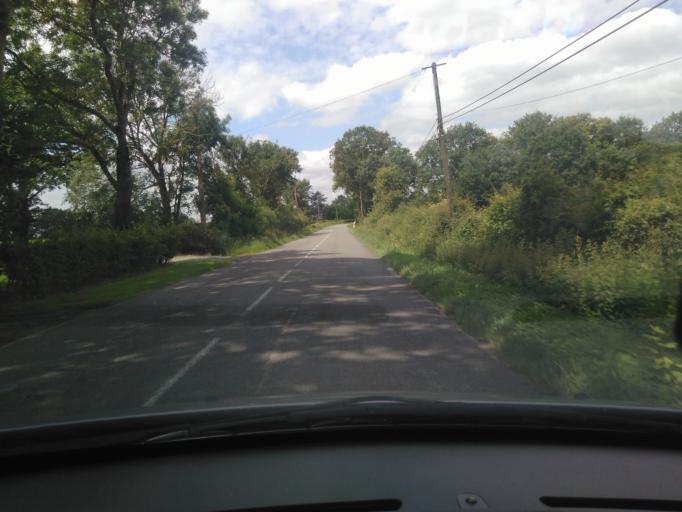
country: FR
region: Pays de la Loire
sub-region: Departement de la Vendee
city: Les Essarts
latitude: 46.7778
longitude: -1.2468
